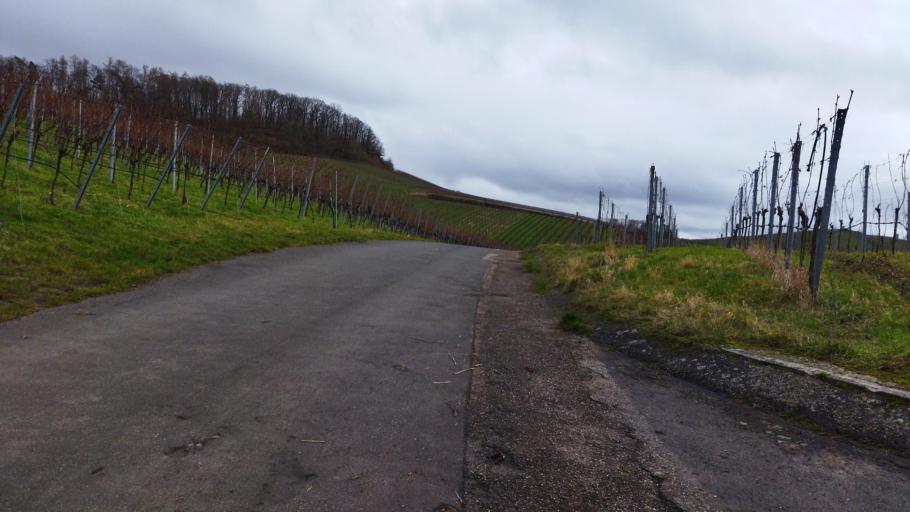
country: DE
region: Baden-Wuerttemberg
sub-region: Regierungsbezirk Stuttgart
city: Heilbronn
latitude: 49.1197
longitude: 9.2303
